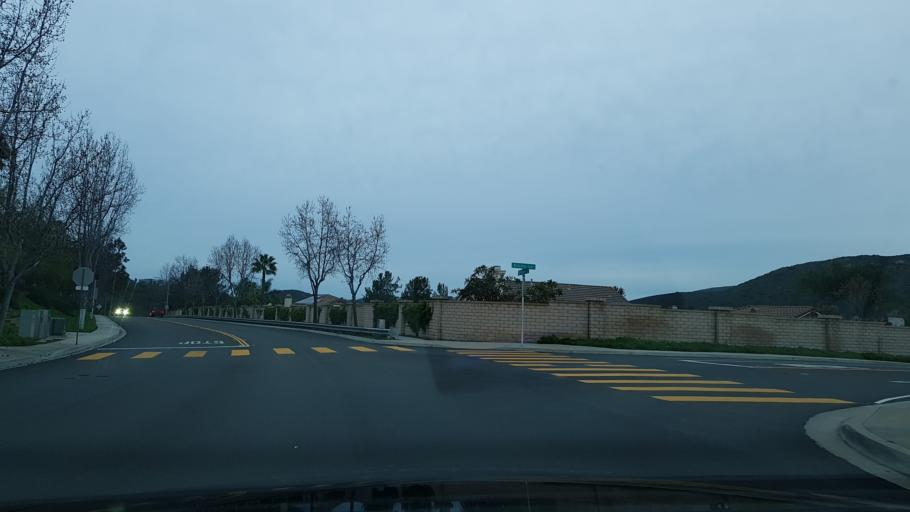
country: US
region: California
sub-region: San Diego County
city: Poway
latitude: 32.9403
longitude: -117.0801
